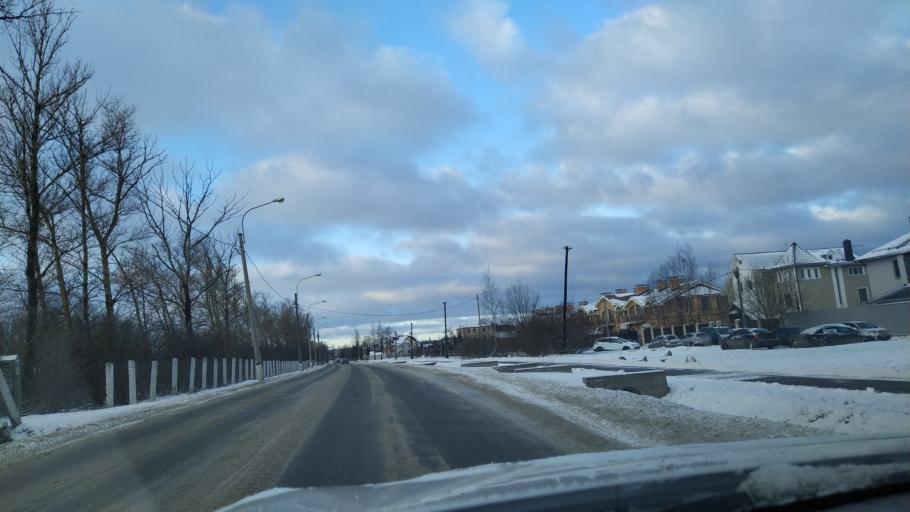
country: RU
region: St.-Petersburg
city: Pushkin
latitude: 59.7317
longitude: 30.3718
